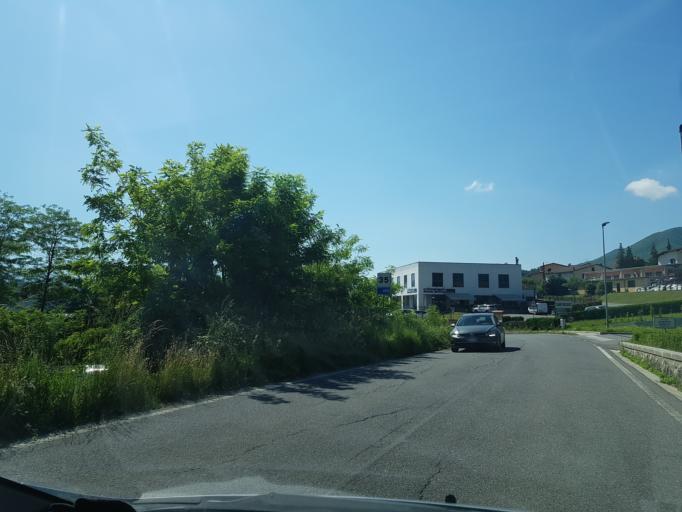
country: IT
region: Tuscany
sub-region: Provincia di Lucca
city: Camporgiano
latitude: 44.1630
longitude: 10.3297
